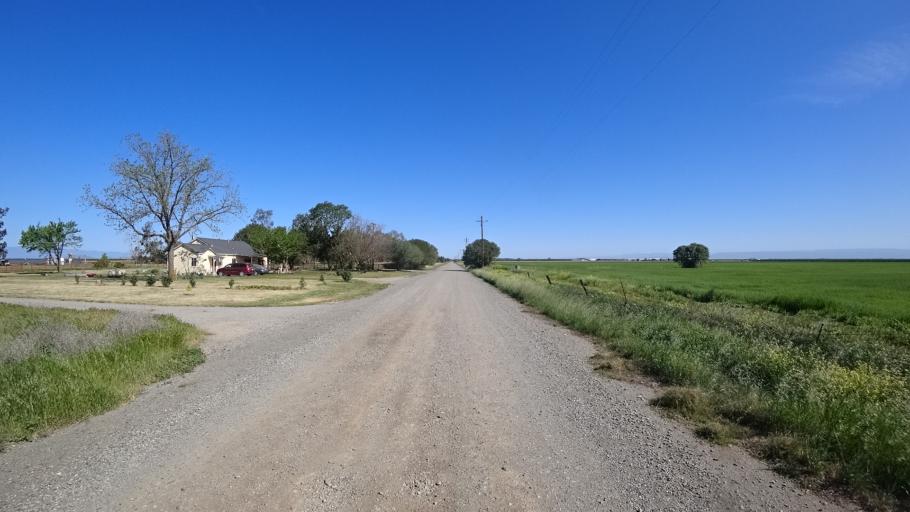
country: US
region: California
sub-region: Glenn County
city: Orland
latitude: 39.6449
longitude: -122.1598
